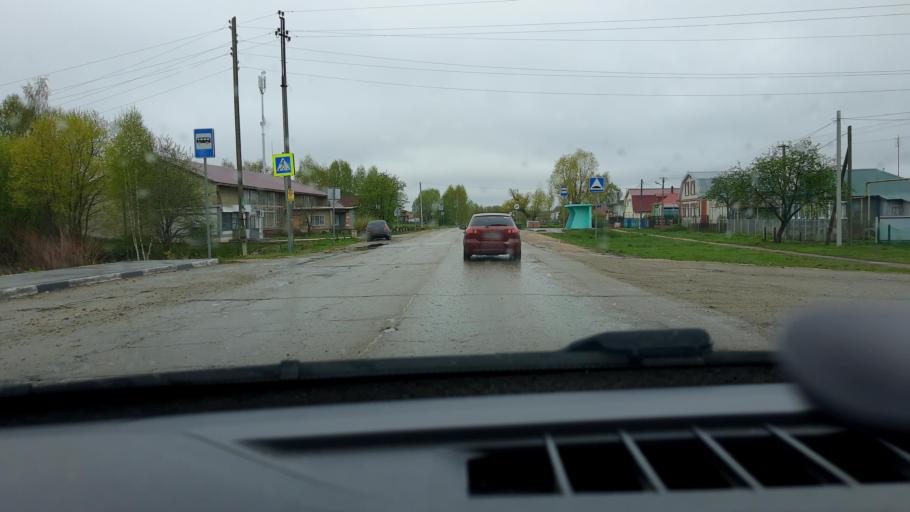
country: RU
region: Nizjnij Novgorod
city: Perevoz
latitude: 55.5931
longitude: 44.6551
